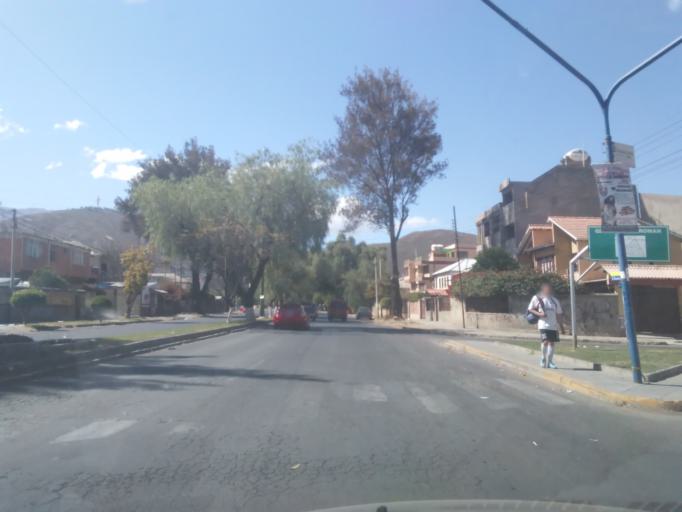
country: BO
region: Cochabamba
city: Cochabamba
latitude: -17.3971
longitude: -66.1452
